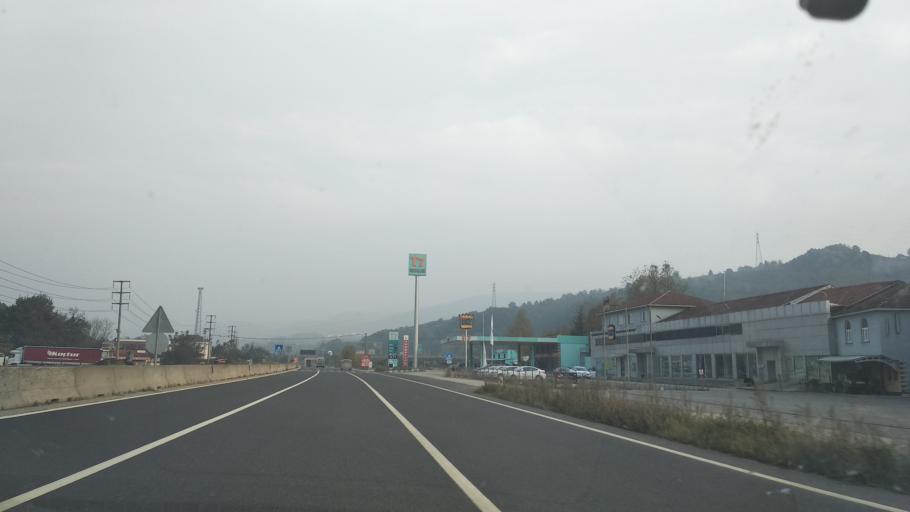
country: TR
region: Duzce
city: Kaynasli
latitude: 40.7885
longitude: 31.2606
